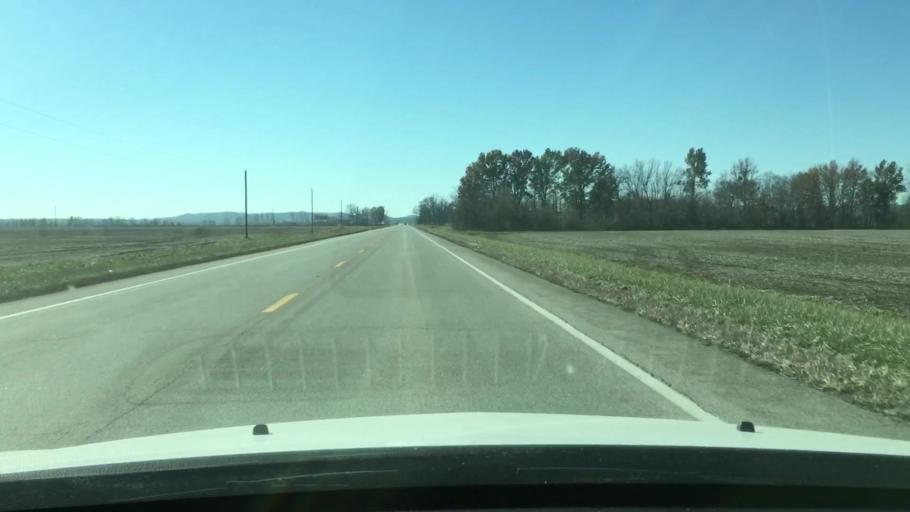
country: US
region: Missouri
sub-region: Pike County
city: Louisiana
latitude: 39.4954
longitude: -91.0038
